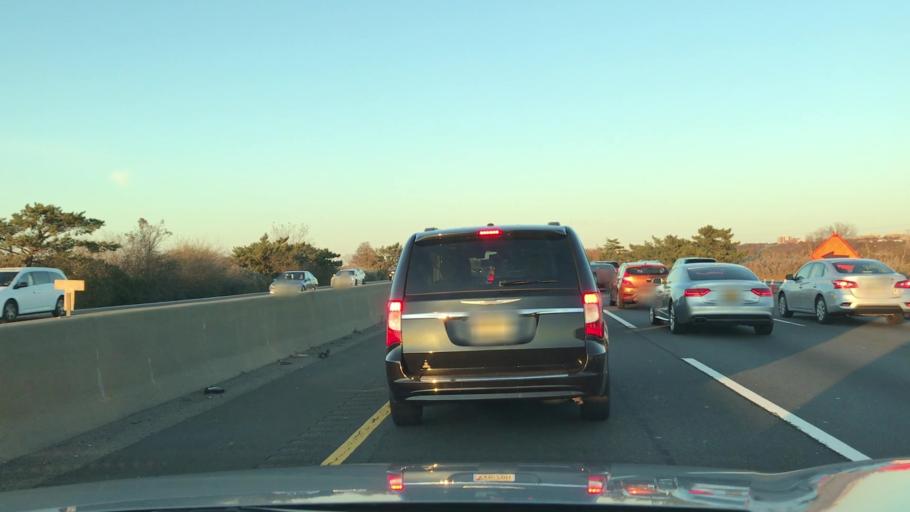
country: US
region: New Jersey
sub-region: Hudson County
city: Secaucus
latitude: 40.7990
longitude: -74.0387
